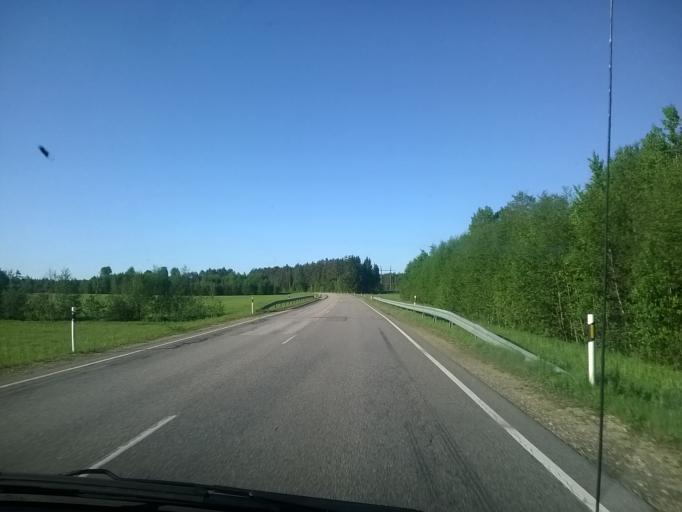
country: EE
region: Valgamaa
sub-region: Valga linn
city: Valga
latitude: 57.8974
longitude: 26.1674
